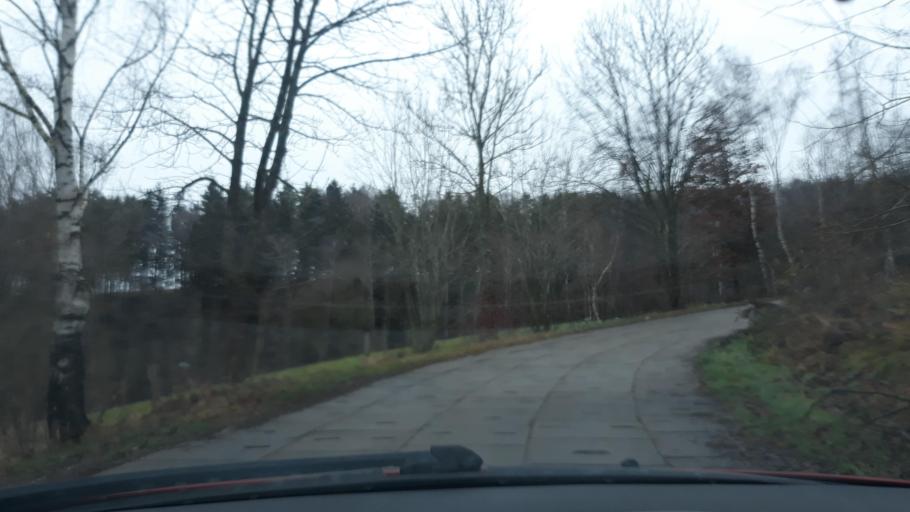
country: DE
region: Saxony
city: Kirchberg
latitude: 50.6483
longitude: 12.5245
